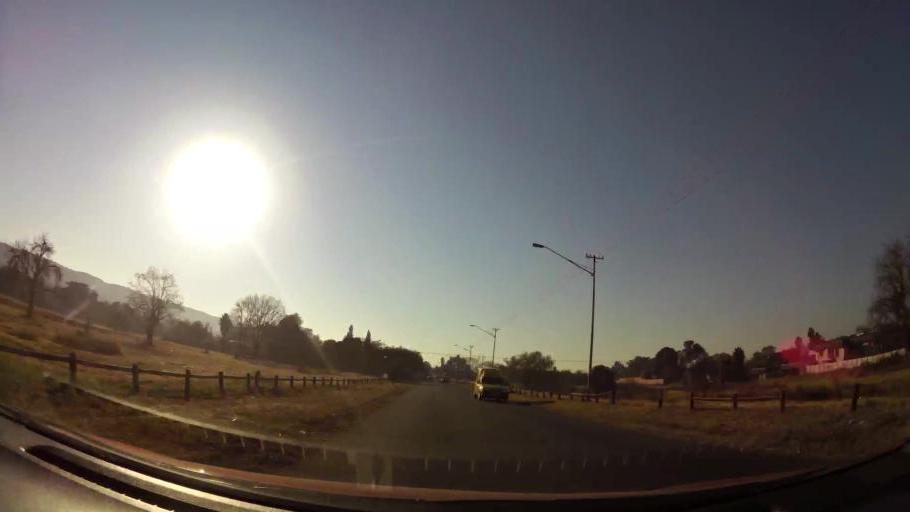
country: ZA
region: Gauteng
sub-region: City of Tshwane Metropolitan Municipality
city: Pretoria
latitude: -25.7055
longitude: 28.1982
